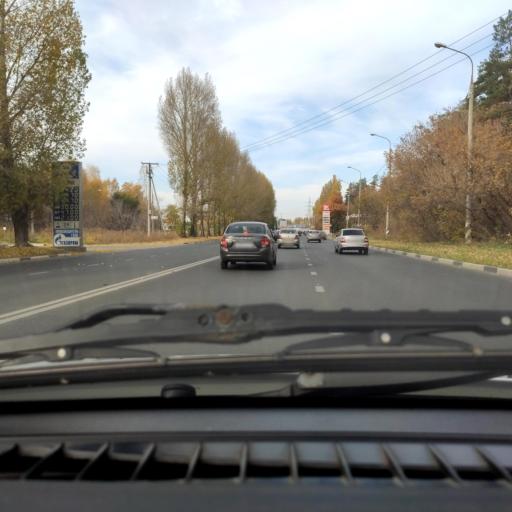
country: RU
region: Samara
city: Zhigulevsk
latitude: 53.5076
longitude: 49.4649
